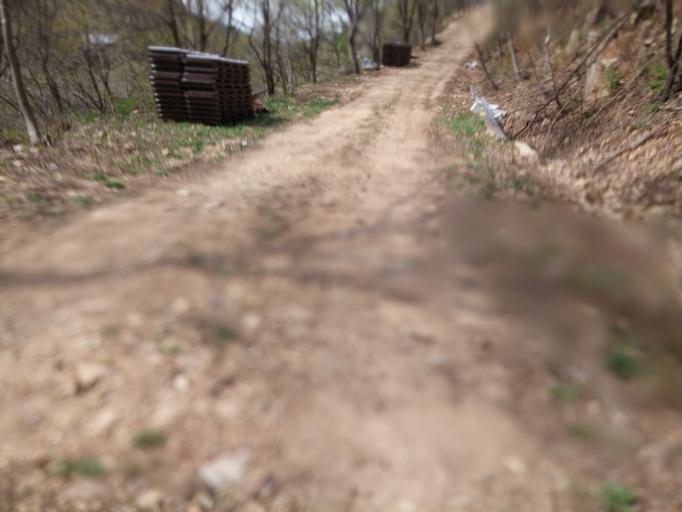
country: KR
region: Chungcheongbuk-do
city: Okcheon
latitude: 36.2404
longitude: 127.5564
